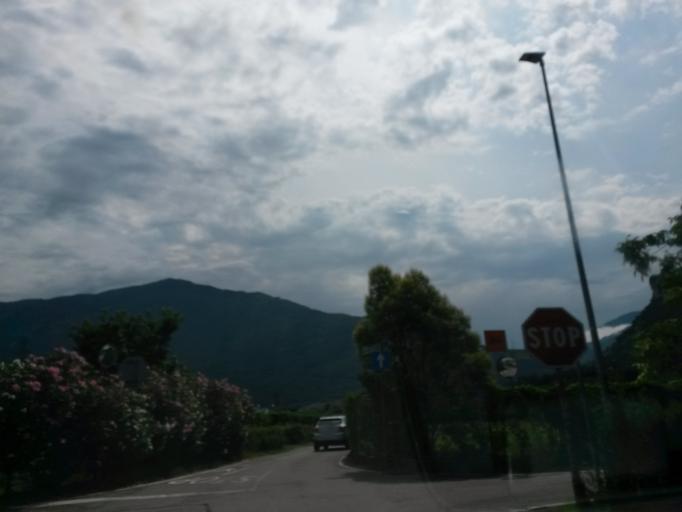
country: IT
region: Trentino-Alto Adige
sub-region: Provincia di Trento
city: Arco
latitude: 45.9011
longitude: 10.8651
